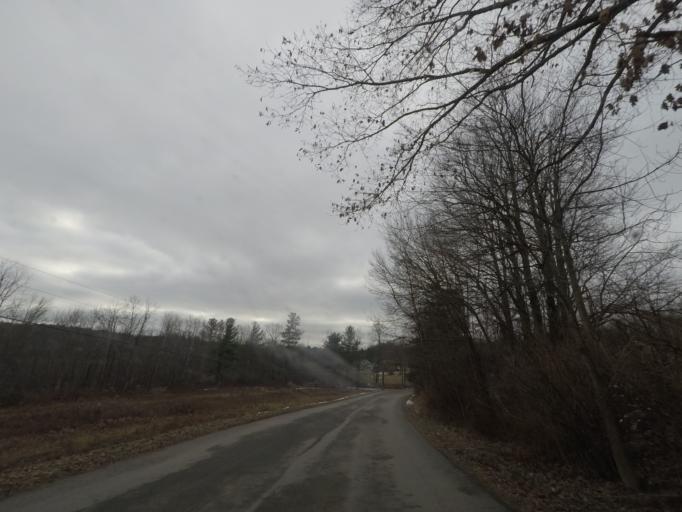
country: US
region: New York
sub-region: Rensselaer County
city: West Sand Lake
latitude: 42.5915
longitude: -73.6406
